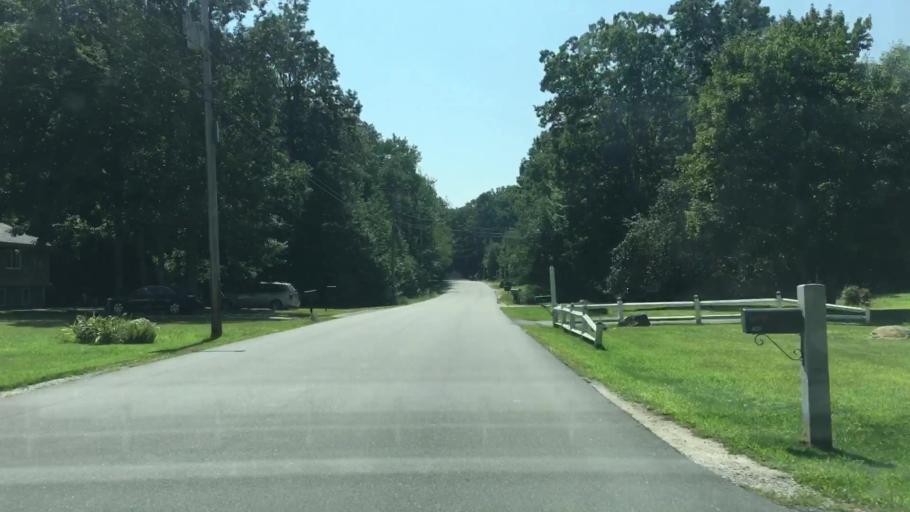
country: US
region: New Hampshire
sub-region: Rockingham County
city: Hampstead
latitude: 42.8910
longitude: -71.2175
